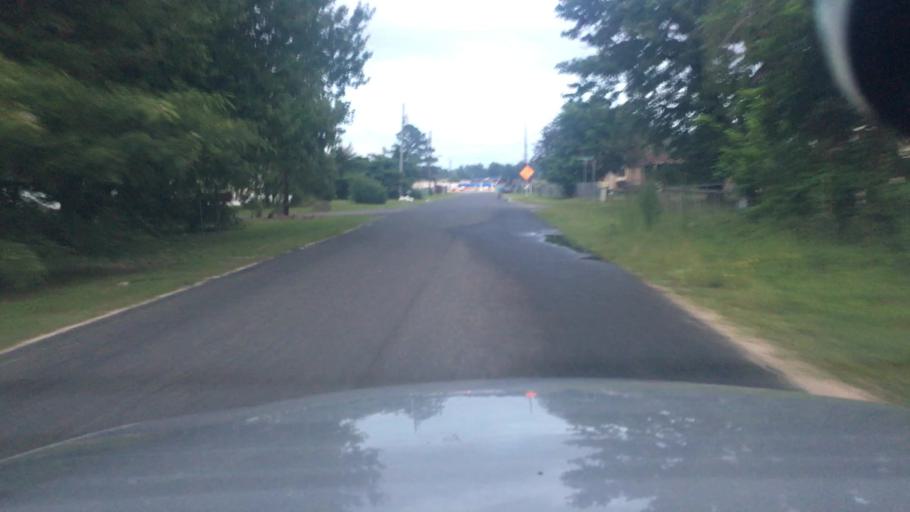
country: US
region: North Carolina
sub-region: Cumberland County
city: Hope Mills
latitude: 34.9834
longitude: -78.9093
